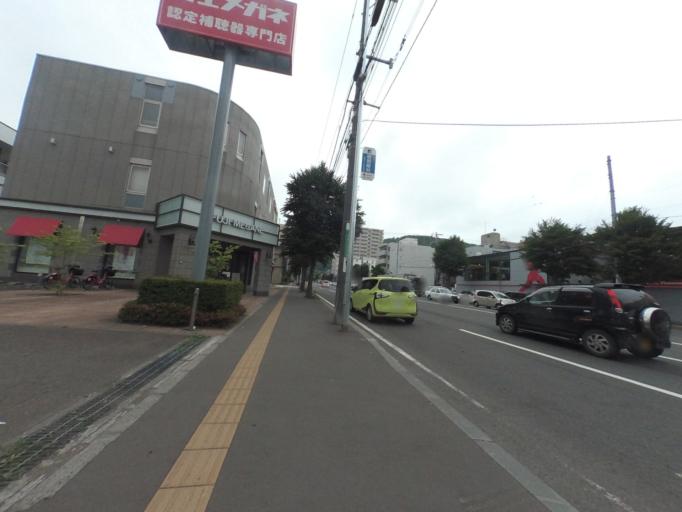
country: JP
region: Hokkaido
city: Sapporo
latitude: 43.0565
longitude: 141.3158
